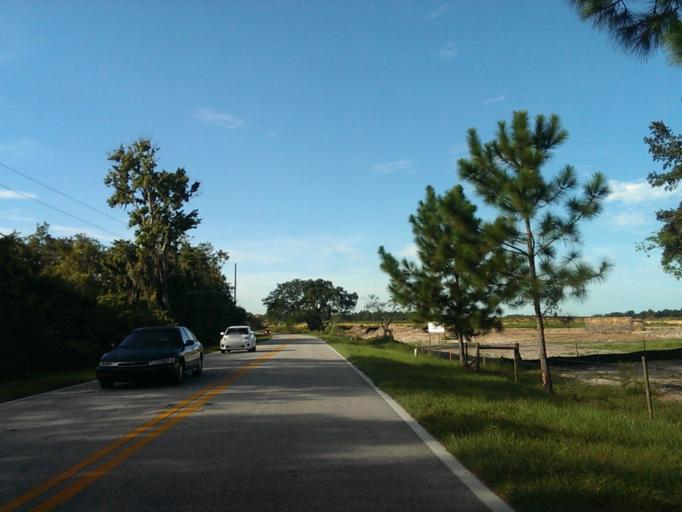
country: US
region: Florida
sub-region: Polk County
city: Citrus Ridge
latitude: 28.4048
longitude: -81.6368
